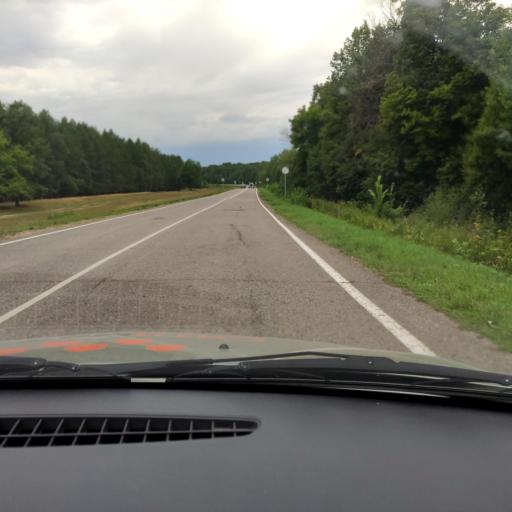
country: RU
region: Bashkortostan
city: Krasnaya Gorka
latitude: 55.2607
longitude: 56.6695
